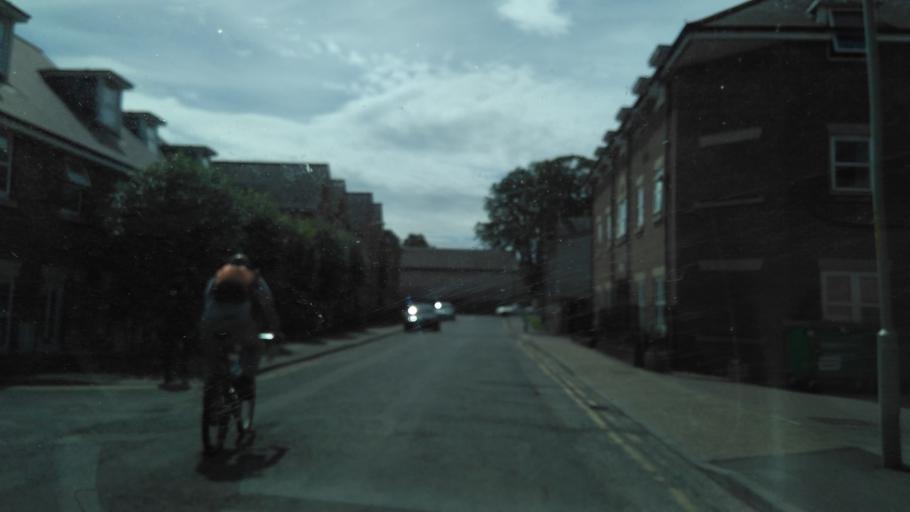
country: GB
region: England
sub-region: Kent
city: Canterbury
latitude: 51.2887
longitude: 1.0943
